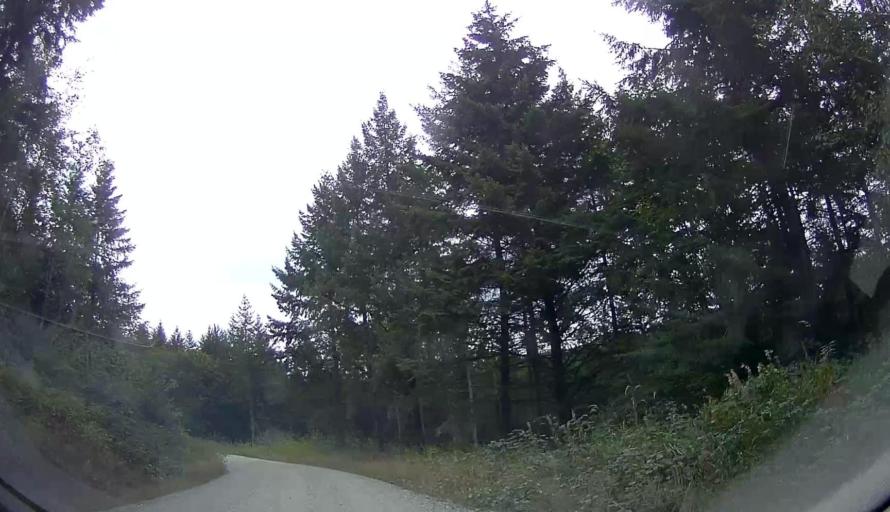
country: US
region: Washington
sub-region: Whatcom County
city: Sudden Valley
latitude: 48.6115
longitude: -122.3811
